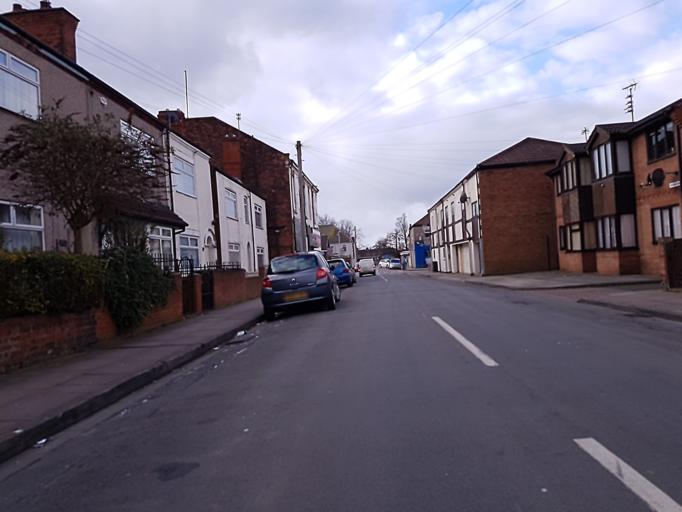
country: GB
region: England
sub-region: North East Lincolnshire
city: Grimsby
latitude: 53.5674
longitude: -0.0623
